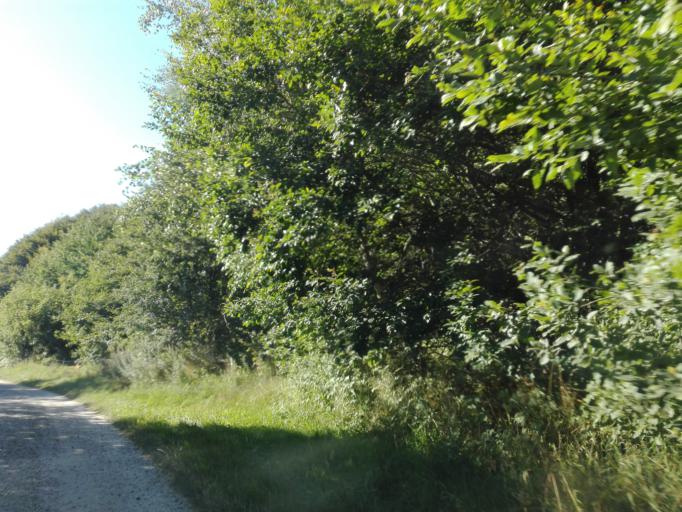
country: DK
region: North Denmark
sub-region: Mariagerfjord Kommune
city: Mariager
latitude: 56.6667
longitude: 9.9530
